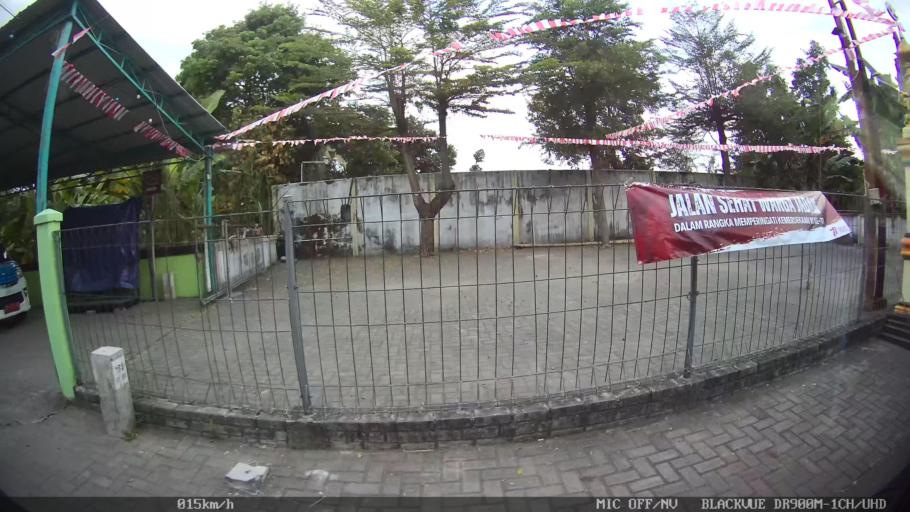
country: ID
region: Daerah Istimewa Yogyakarta
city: Kasihan
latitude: -7.8211
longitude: 110.3268
